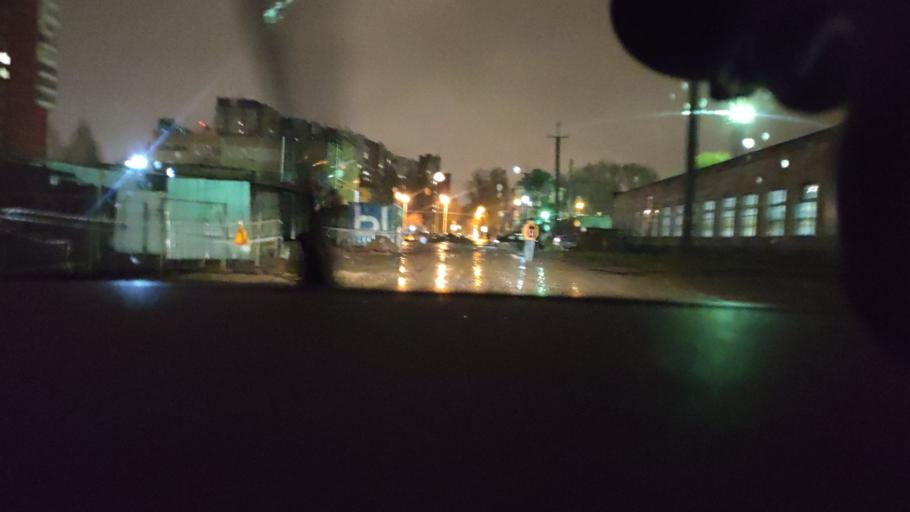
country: RU
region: Perm
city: Perm
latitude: 57.9779
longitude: 56.1927
